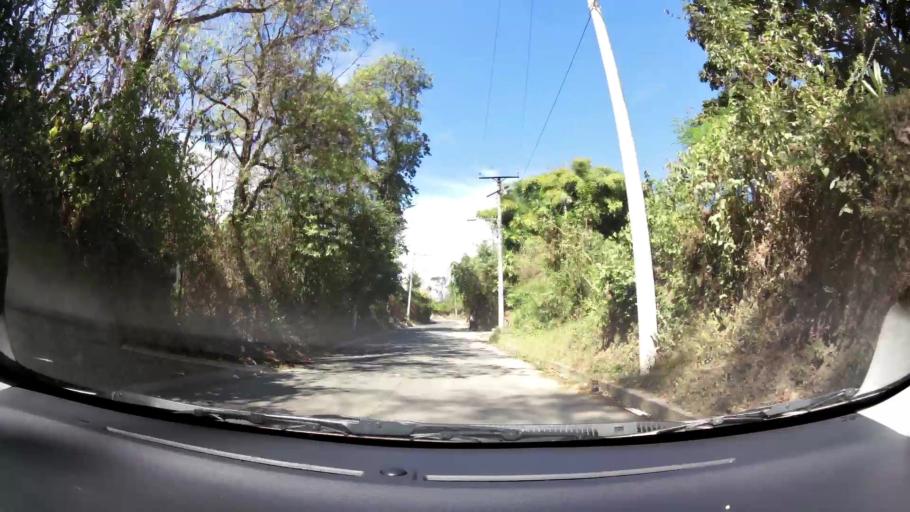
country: SV
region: San Salvador
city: Apopa
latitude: 13.8130
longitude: -89.1743
